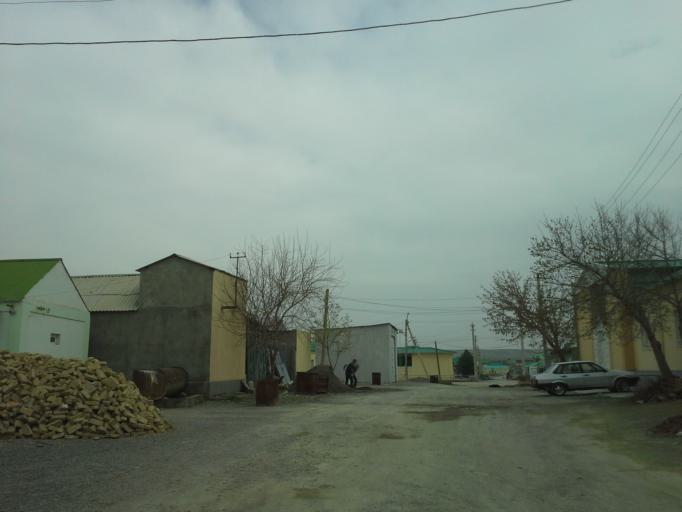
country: TM
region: Ahal
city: Abadan
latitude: 37.9775
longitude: 58.2209
